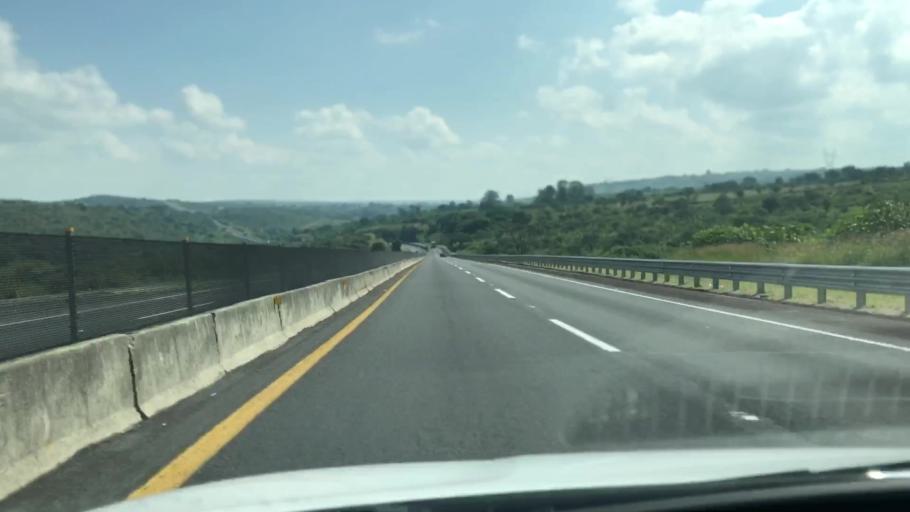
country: MX
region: Jalisco
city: Zapotlanejo
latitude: 20.6668
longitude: -103.0368
